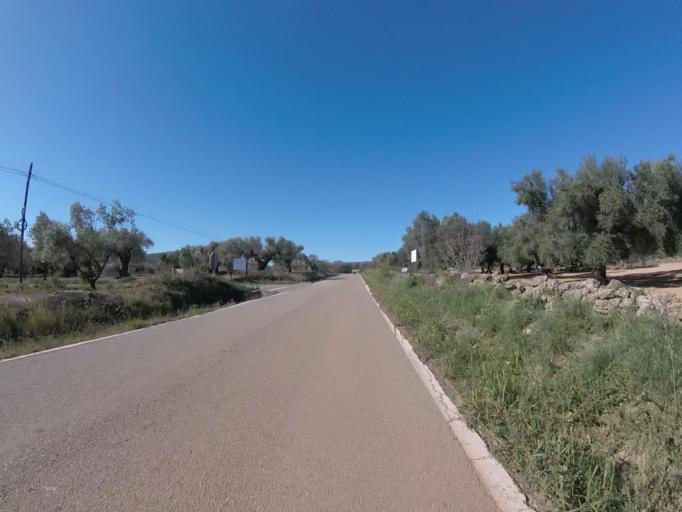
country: ES
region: Valencia
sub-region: Provincia de Castello
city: Chert/Xert
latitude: 40.4523
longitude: 0.1239
